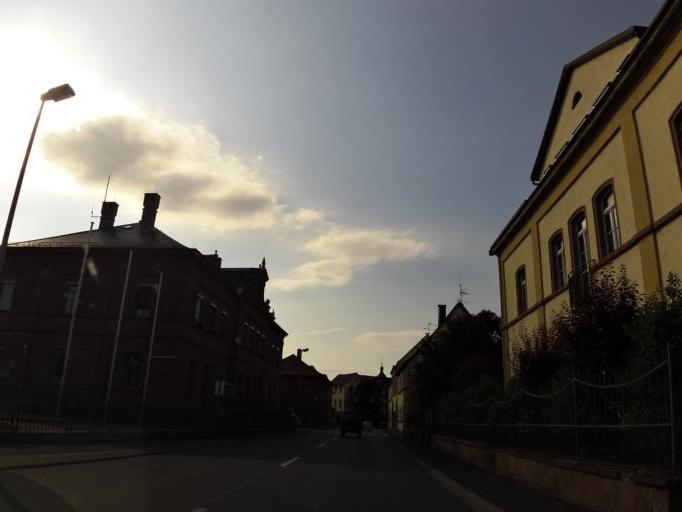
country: DE
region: Bavaria
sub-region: Regierungsbezirk Unterfranken
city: Marktheidenfeld
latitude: 49.8428
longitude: 9.6037
